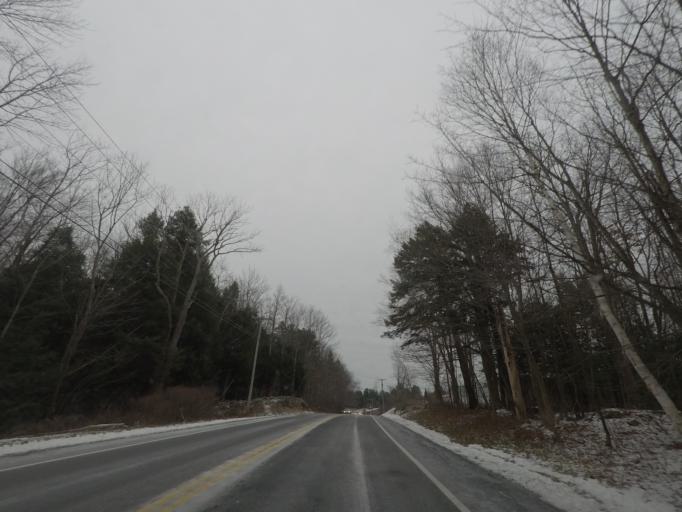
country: US
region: New York
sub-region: Rensselaer County
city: Hoosick Falls
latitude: 42.7695
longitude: -73.4212
